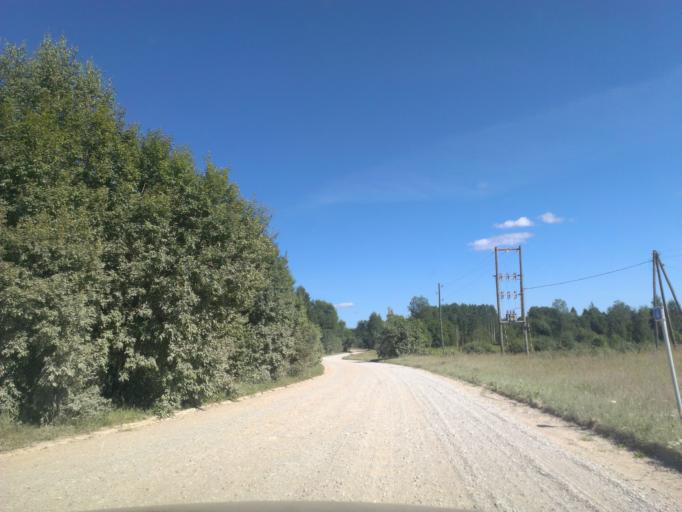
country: LV
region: Malpils
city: Malpils
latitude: 57.0144
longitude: 25.0067
